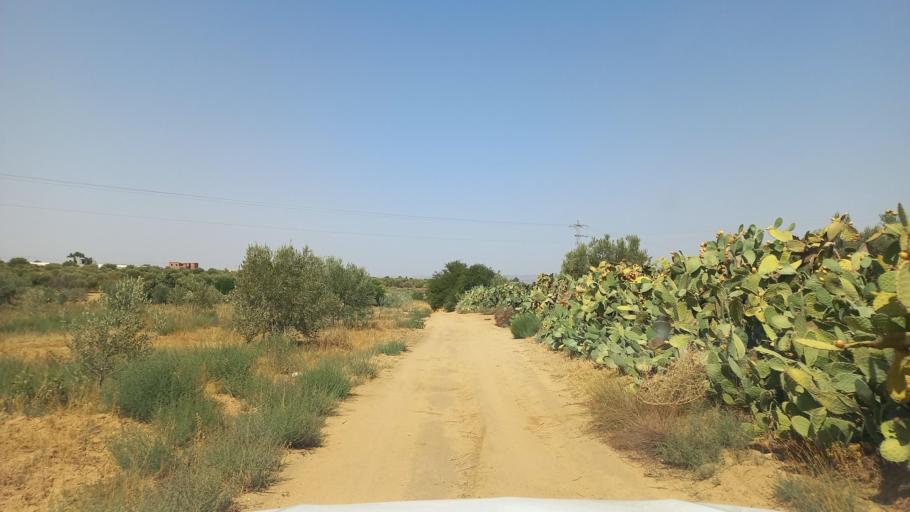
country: TN
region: Al Qasrayn
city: Kasserine
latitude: 35.2425
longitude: 9.0523
